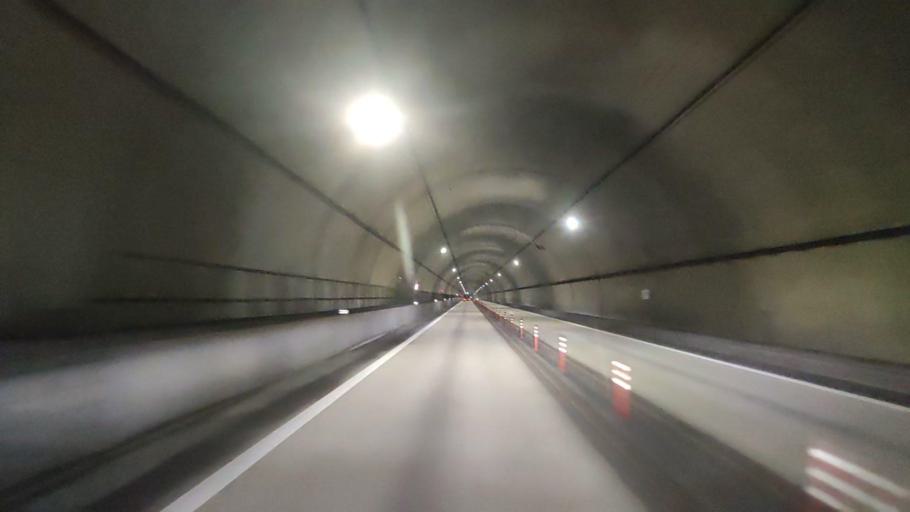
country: JP
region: Wakayama
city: Tanabe
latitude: 33.5425
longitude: 135.5270
